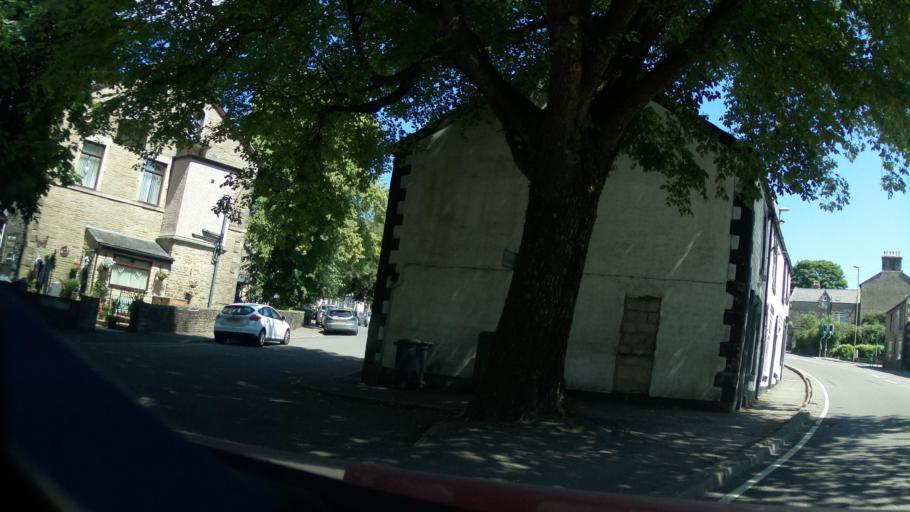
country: GB
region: England
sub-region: Derbyshire
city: Buxton
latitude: 53.2625
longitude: -1.9032
